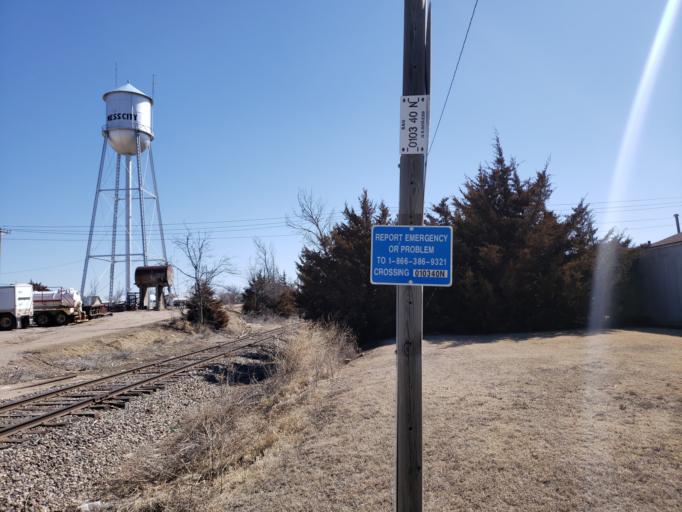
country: US
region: Kansas
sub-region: Ness County
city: Ness City
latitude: 38.4517
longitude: -99.9091
